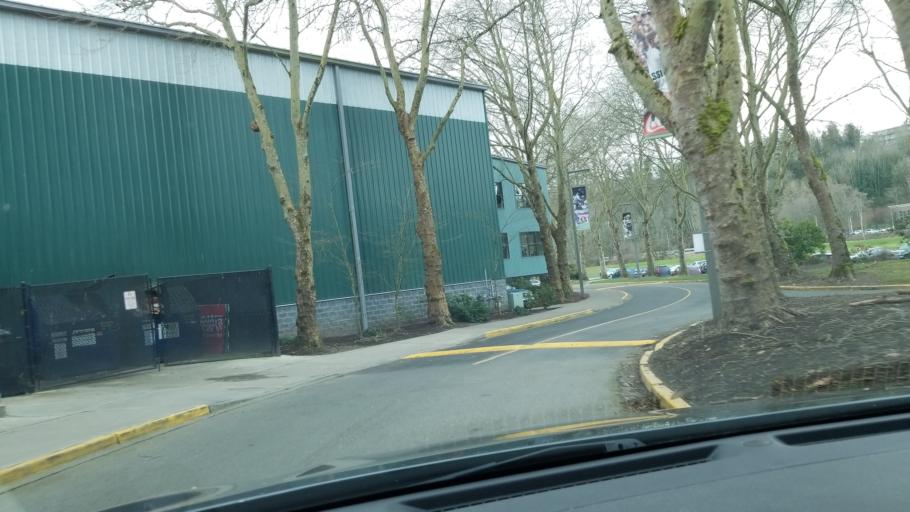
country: US
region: Washington
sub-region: King County
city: Tukwila
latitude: 47.4704
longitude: -122.2498
